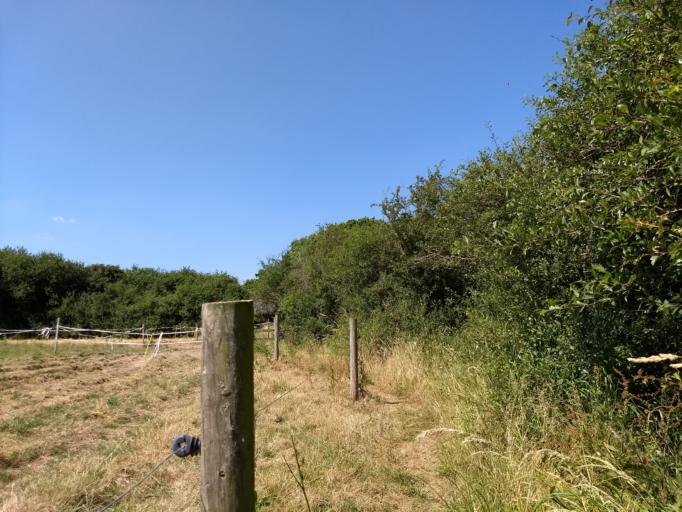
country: GB
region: England
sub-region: Isle of Wight
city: Gurnard
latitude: 50.7286
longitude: -1.3613
